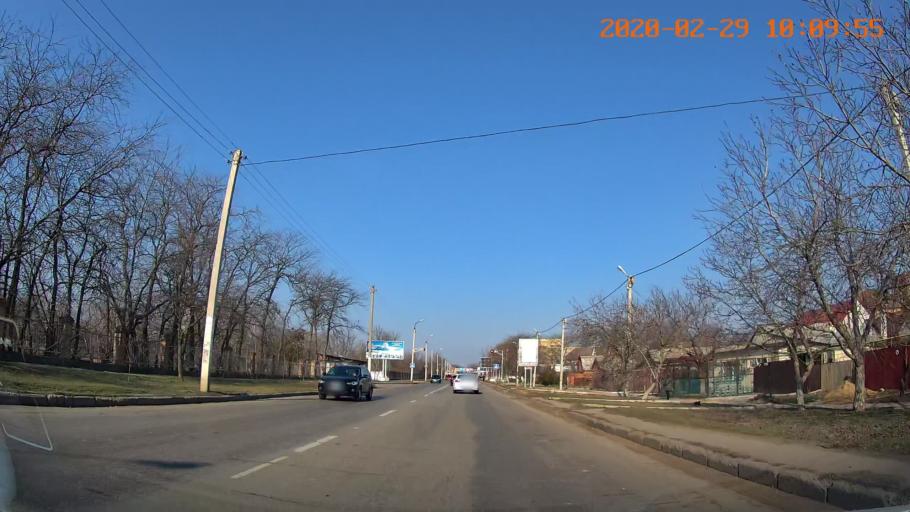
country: MD
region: Telenesti
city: Tiraspolul Nou
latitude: 46.8305
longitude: 29.6484
